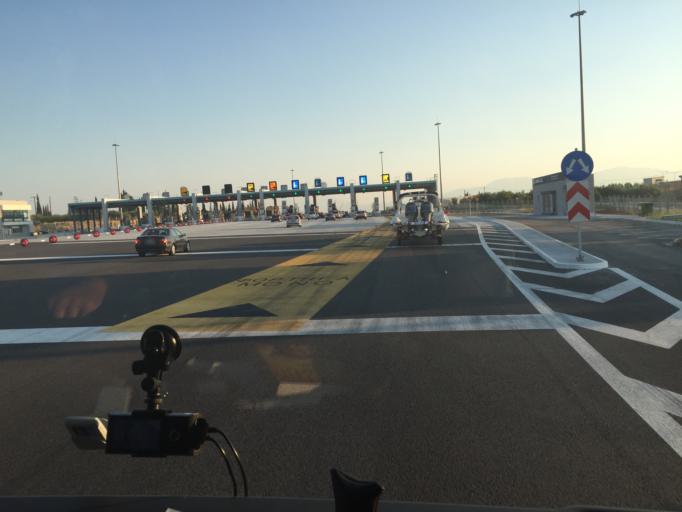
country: GR
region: Peloponnese
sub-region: Nomos Korinthias
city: Moulki
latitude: 37.9952
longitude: 22.7357
